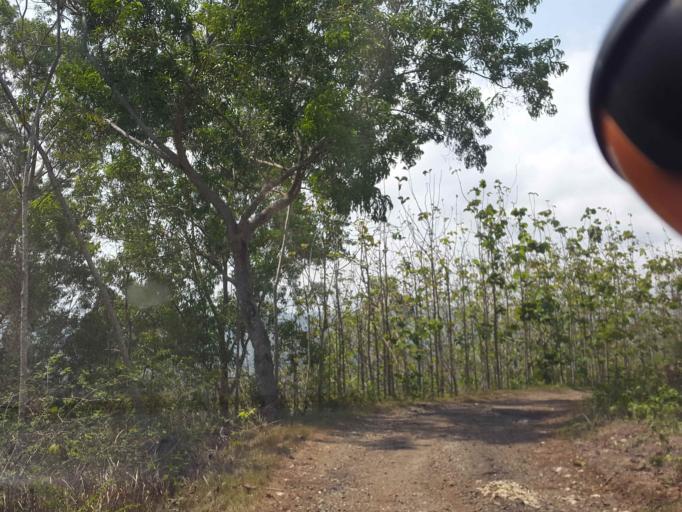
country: ID
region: East Java
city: Krajan
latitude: -8.2256
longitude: 111.1197
